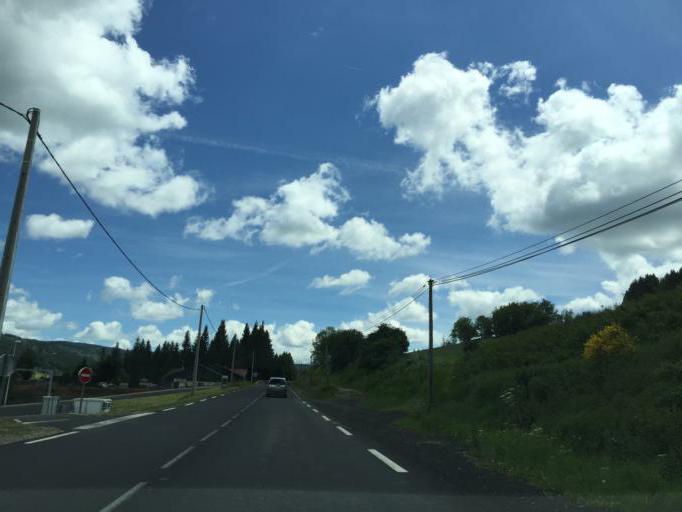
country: FR
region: Rhone-Alpes
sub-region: Departement de la Loire
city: Usson-en-Forez
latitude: 45.5227
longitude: 3.9113
